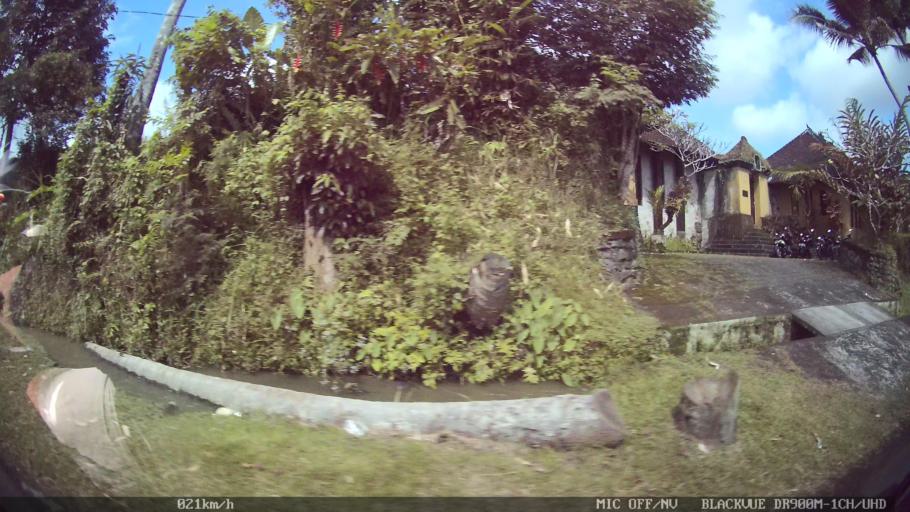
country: ID
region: Bali
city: Banjar Pesalakan
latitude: -8.5114
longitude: 115.3062
